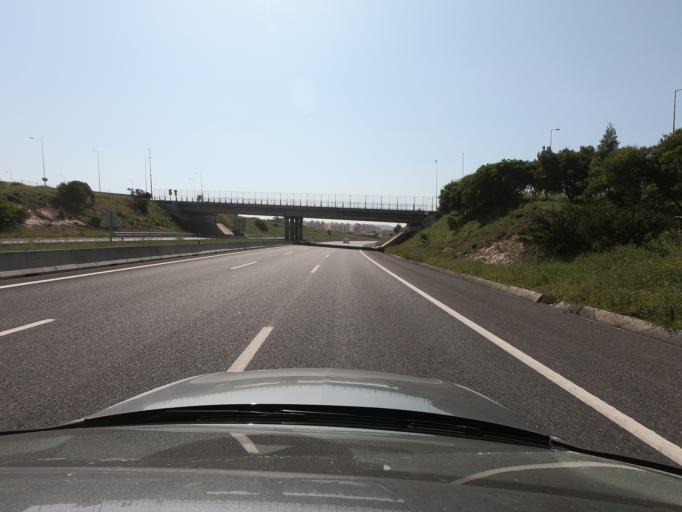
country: PT
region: Lisbon
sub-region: Sintra
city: Cacem
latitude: 38.7810
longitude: -9.2896
